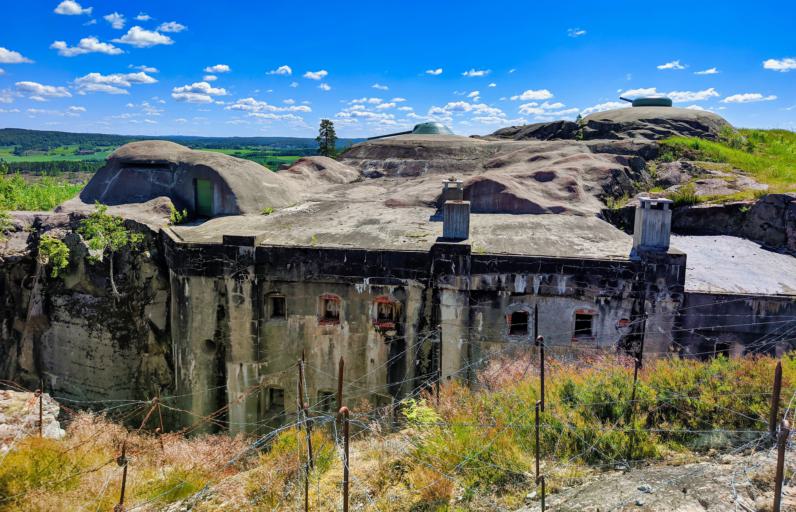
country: NO
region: Ostfold
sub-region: Eidsberg
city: Mysen
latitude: 59.5630
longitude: 11.3443
